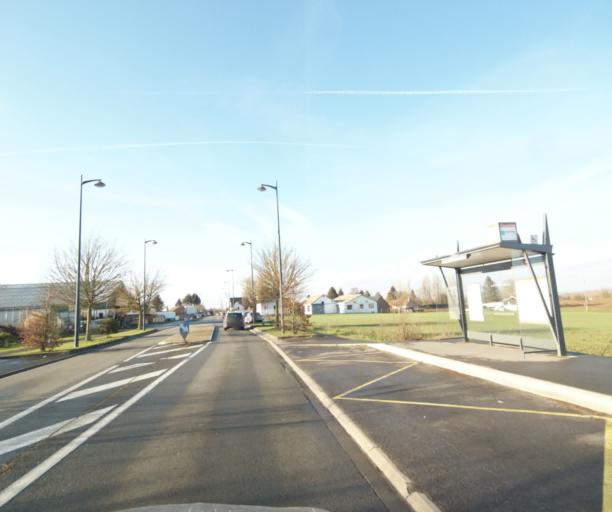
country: FR
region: Nord-Pas-de-Calais
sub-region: Departement du Nord
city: Saultain
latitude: 50.3346
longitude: 3.5881
